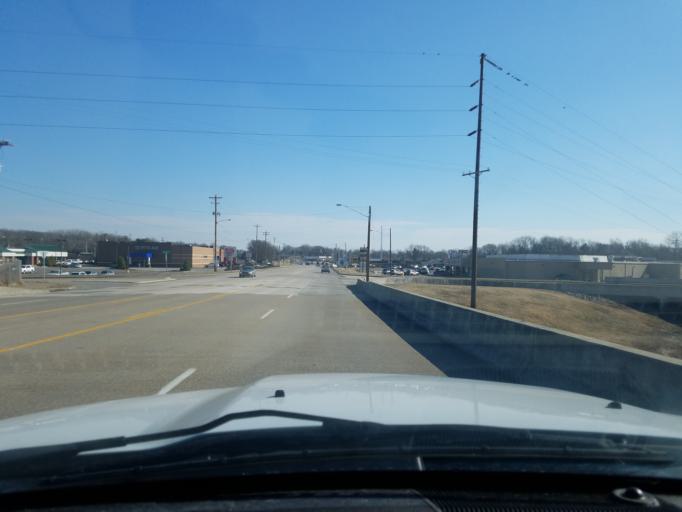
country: US
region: Kentucky
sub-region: Henderson County
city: Henderson
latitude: 37.8335
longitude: -87.5740
